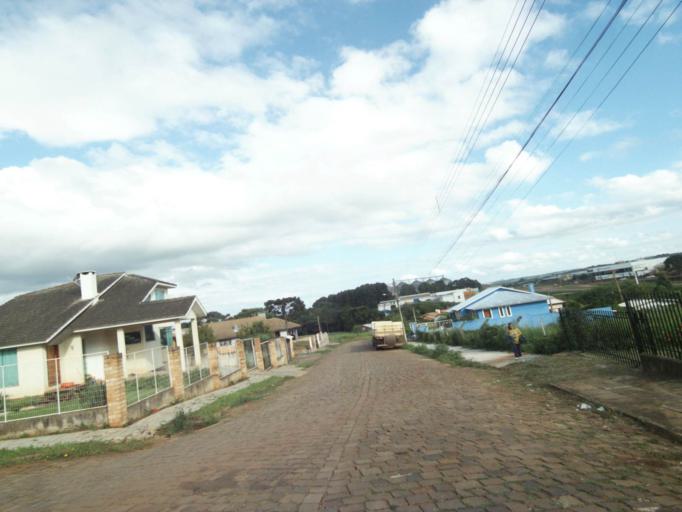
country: BR
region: Rio Grande do Sul
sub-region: Lagoa Vermelha
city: Lagoa Vermelha
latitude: -28.2068
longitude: -51.5149
